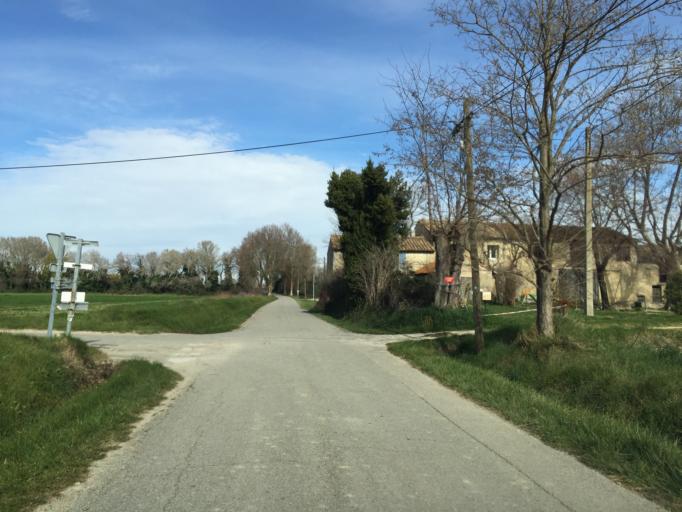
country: FR
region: Provence-Alpes-Cote d'Azur
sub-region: Departement du Vaucluse
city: Caderousse
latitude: 44.1320
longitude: 4.7415
